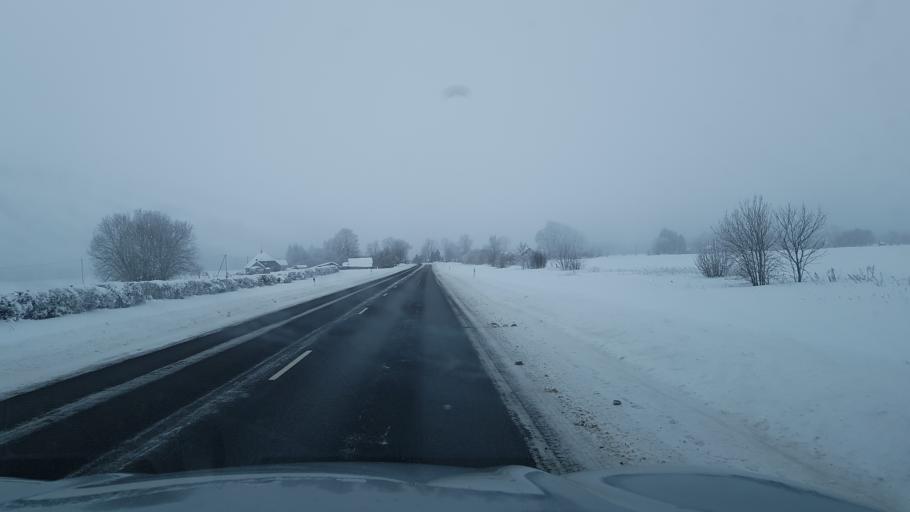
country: EE
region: Ida-Virumaa
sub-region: Johvi vald
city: Johvi
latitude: 59.3215
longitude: 27.3969
